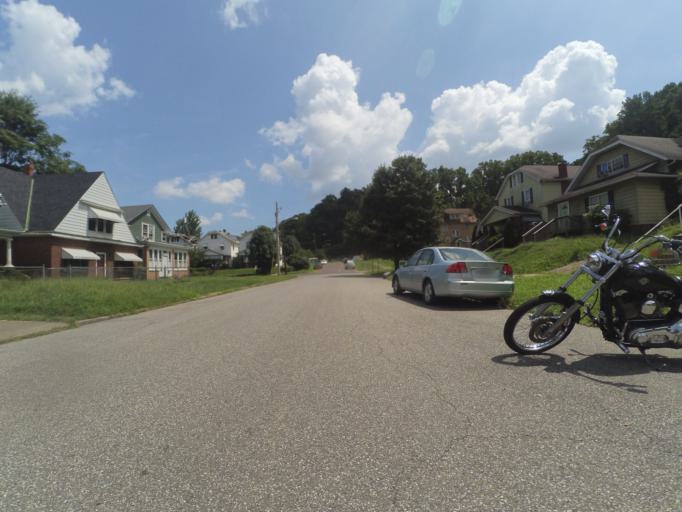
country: US
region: West Virginia
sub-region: Cabell County
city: Huntington
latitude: 38.4152
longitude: -82.4173
